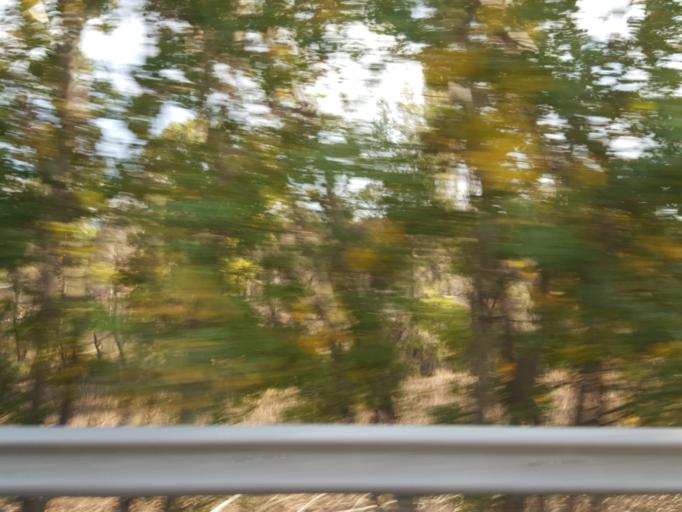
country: TR
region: Corum
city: Alaca
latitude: 40.3271
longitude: 34.7031
